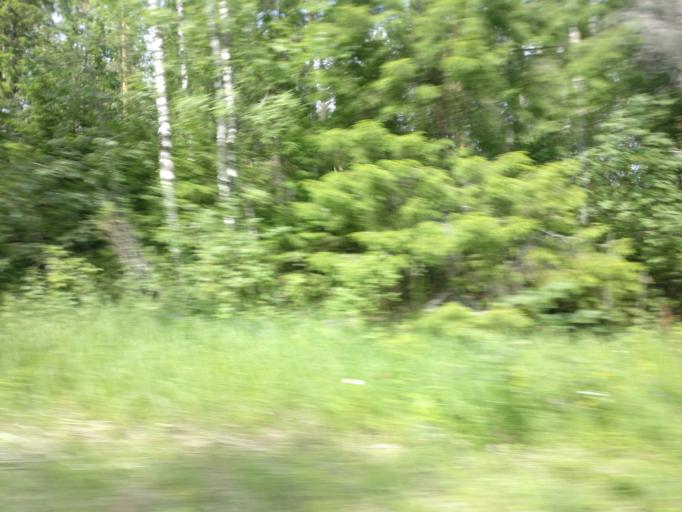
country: FI
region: Southern Savonia
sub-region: Savonlinna
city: Savonlinna
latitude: 61.9848
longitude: 28.8019
